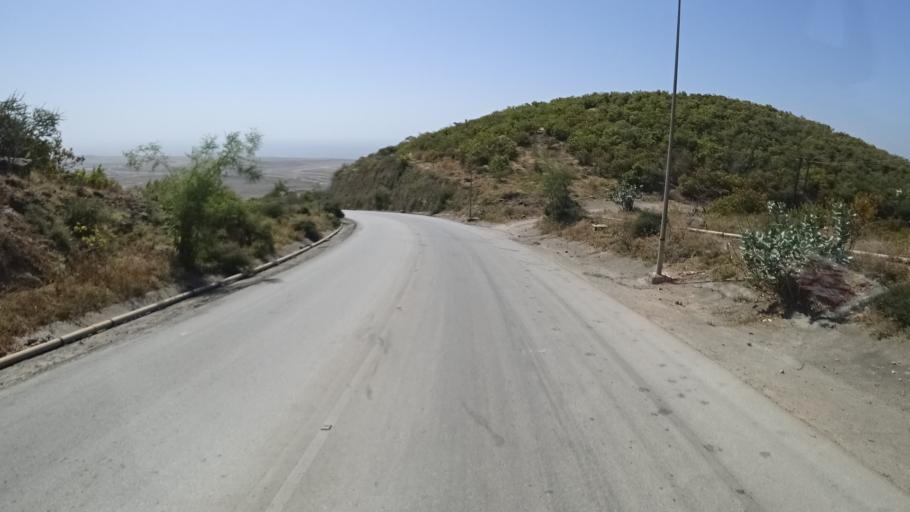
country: OM
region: Zufar
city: Salalah
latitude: 17.0695
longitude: 54.4467
